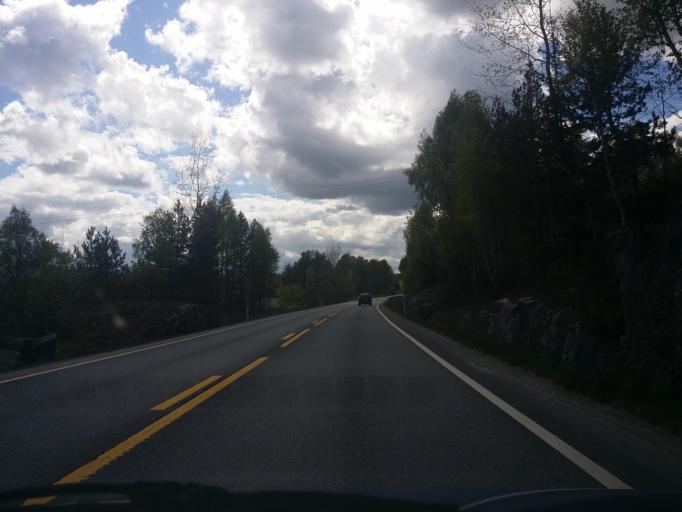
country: NO
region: Buskerud
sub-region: Modum
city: Vikersund
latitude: 59.9524
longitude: 9.9742
